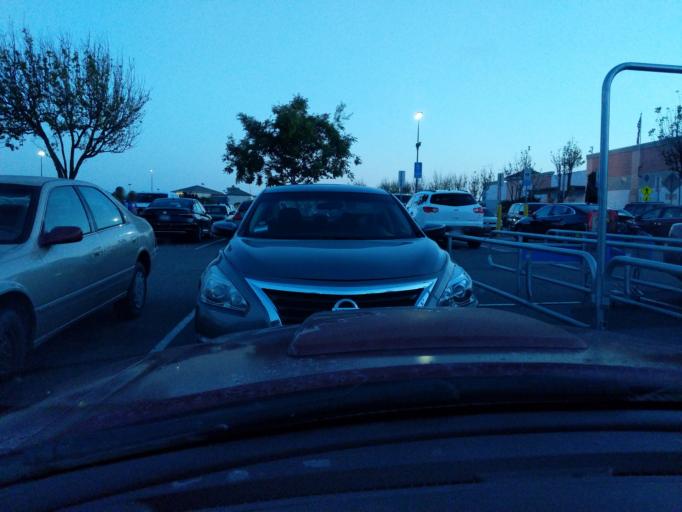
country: US
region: California
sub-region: Monterey County
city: Boronda
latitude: 36.7059
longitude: -121.6678
